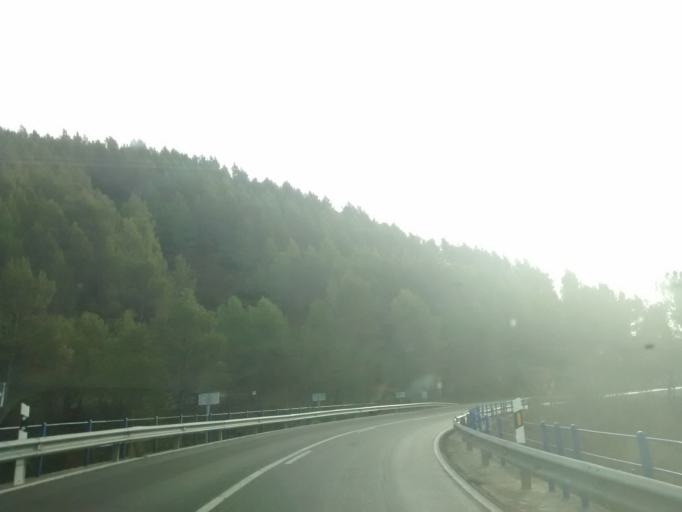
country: ES
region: Aragon
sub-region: Provincia de Zaragoza
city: Undues de Lerda
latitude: 42.6148
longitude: -1.1080
